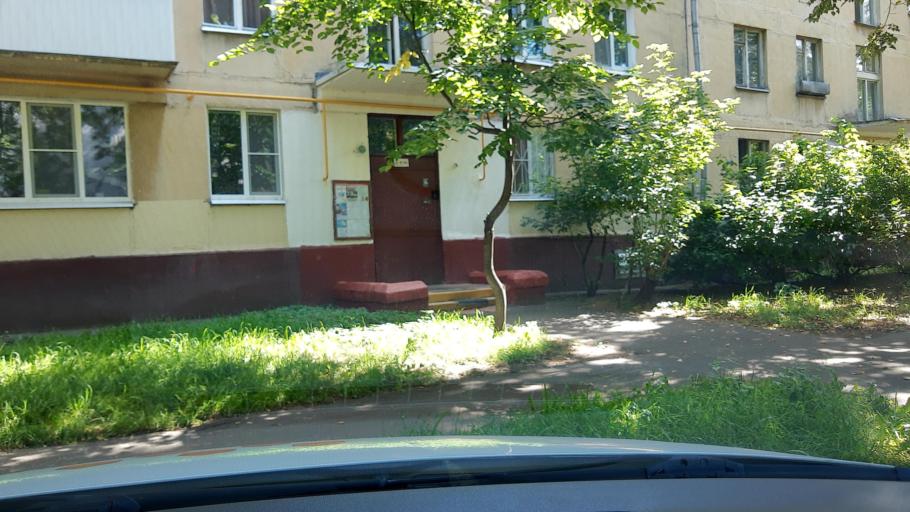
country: RU
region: Moscow
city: Novyye Kuz'minki
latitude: 55.6949
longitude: 37.7603
